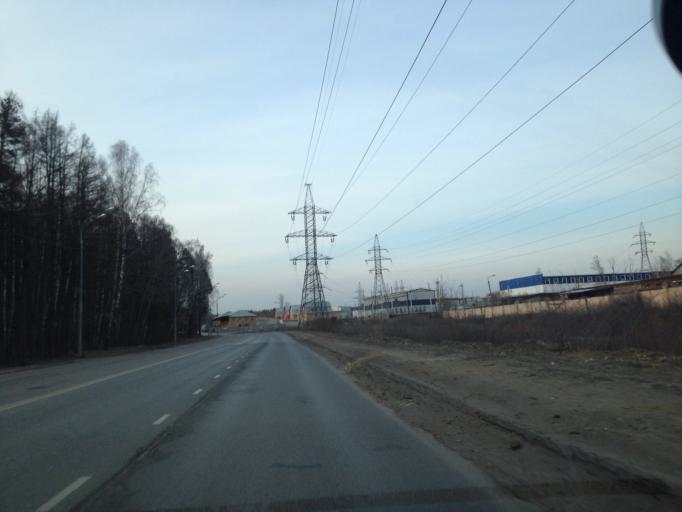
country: RU
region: Moscow
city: Vostochnyy
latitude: 55.7958
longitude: 37.8963
